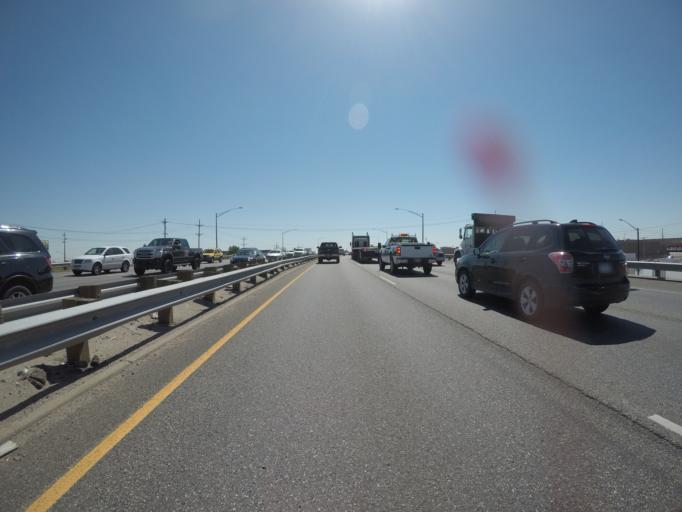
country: US
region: Colorado
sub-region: Adams County
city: Commerce City
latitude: 39.7799
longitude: -104.9325
